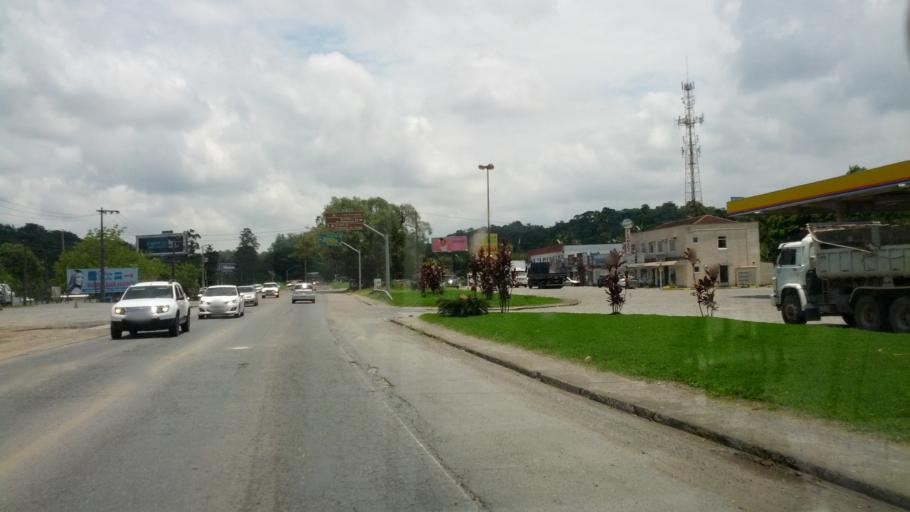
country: BR
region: Santa Catarina
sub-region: Blumenau
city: Blumenau
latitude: -26.8822
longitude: -49.1397
